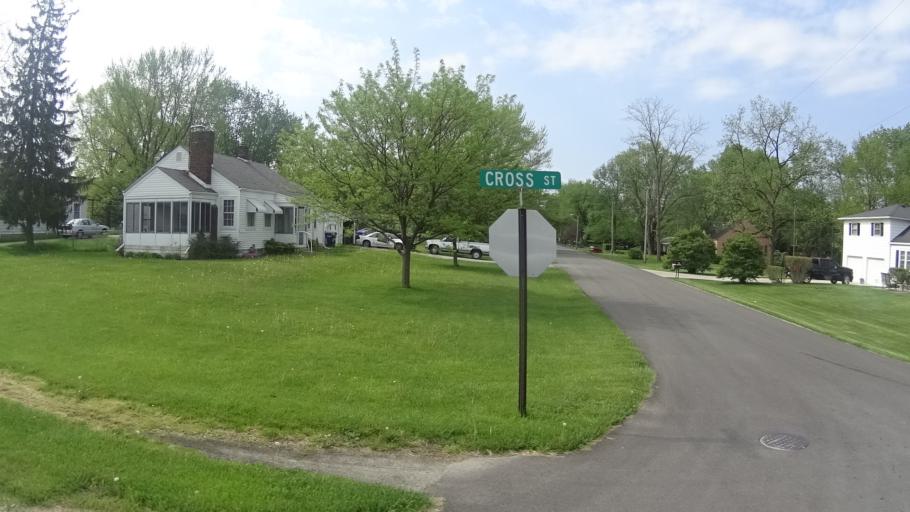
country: US
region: Indiana
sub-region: Madison County
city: Anderson
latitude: 40.1351
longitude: -85.6898
